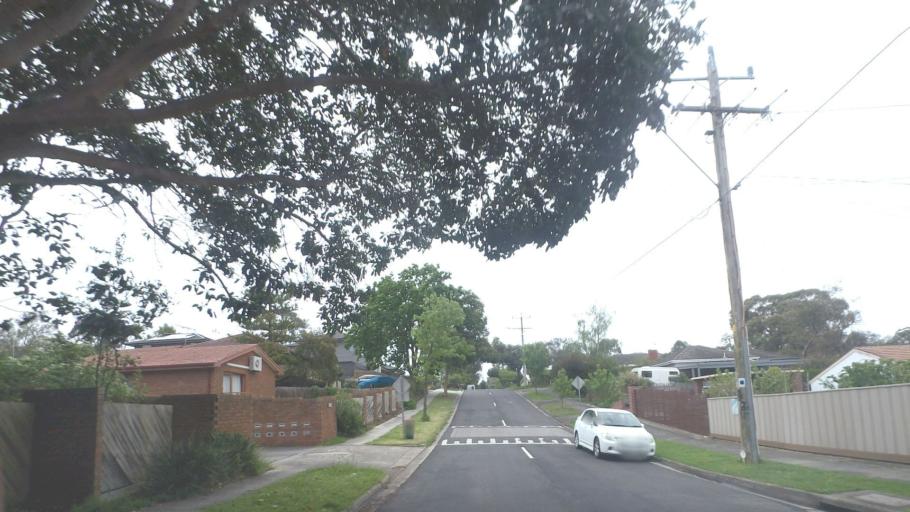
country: AU
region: Victoria
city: Mitcham
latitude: -37.8051
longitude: 145.1952
